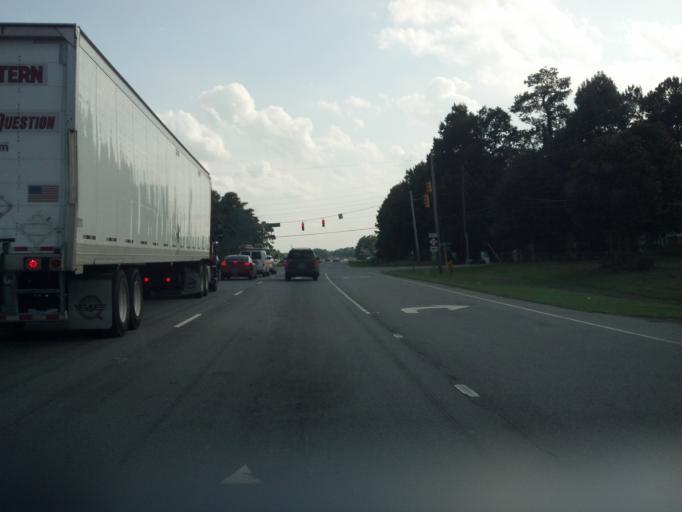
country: US
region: North Carolina
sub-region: Pitt County
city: Greenville
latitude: 35.6489
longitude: -77.3671
